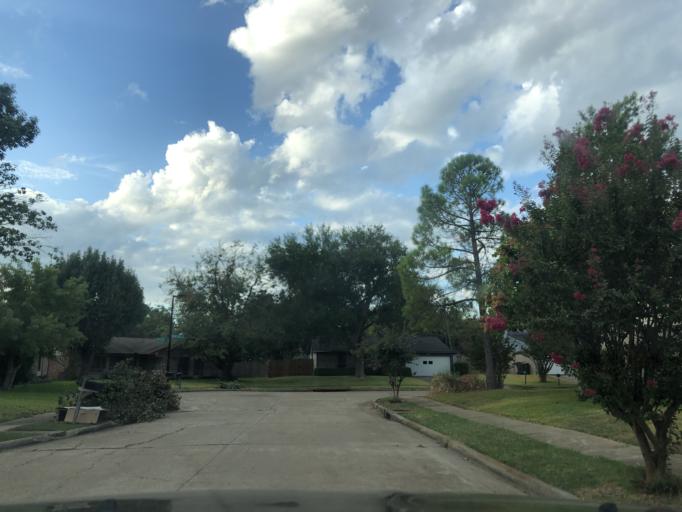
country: US
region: Texas
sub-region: Dallas County
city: Garland
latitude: 32.8724
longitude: -96.6541
